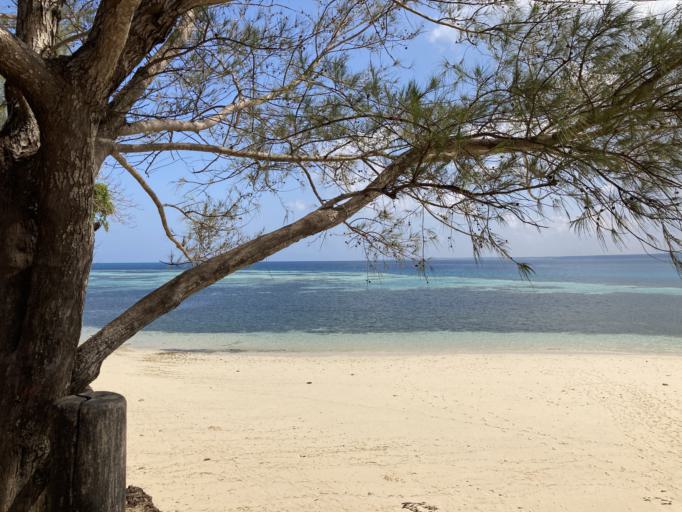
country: TZ
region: Zanzibar Urban/West
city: Zanzibar
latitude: -6.1205
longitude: 39.1689
